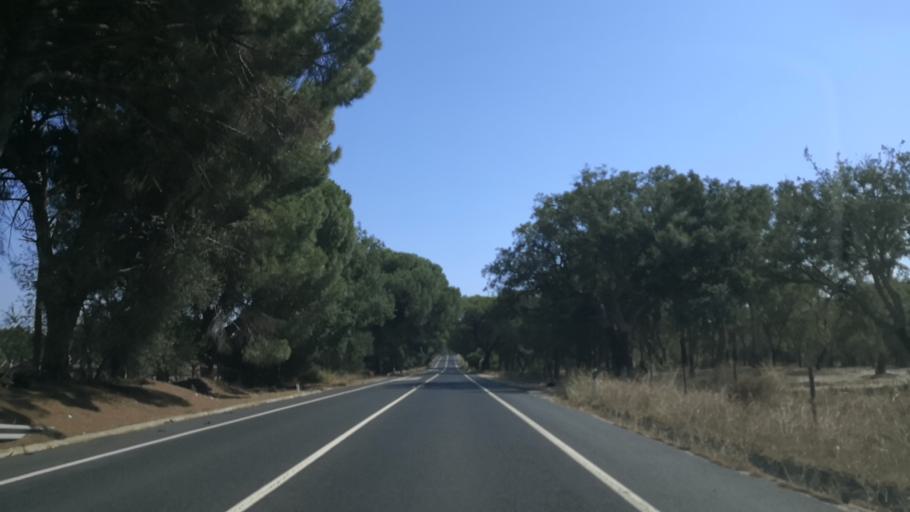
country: PT
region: Evora
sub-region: Vendas Novas
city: Vendas Novas
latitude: 38.7082
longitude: -8.6145
